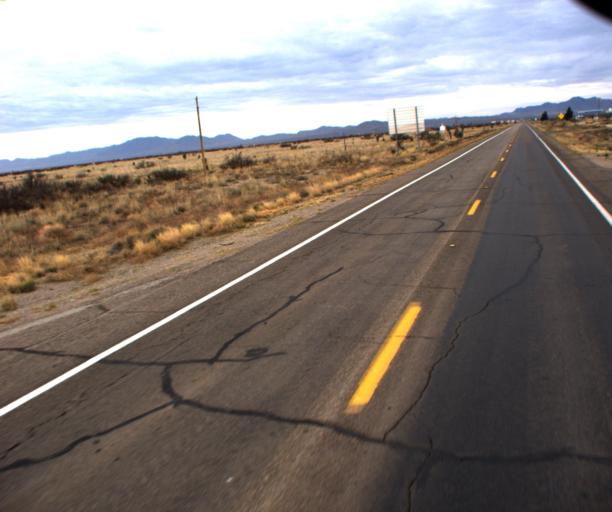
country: US
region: Arizona
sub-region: Cochise County
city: Willcox
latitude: 32.2244
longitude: -109.8692
